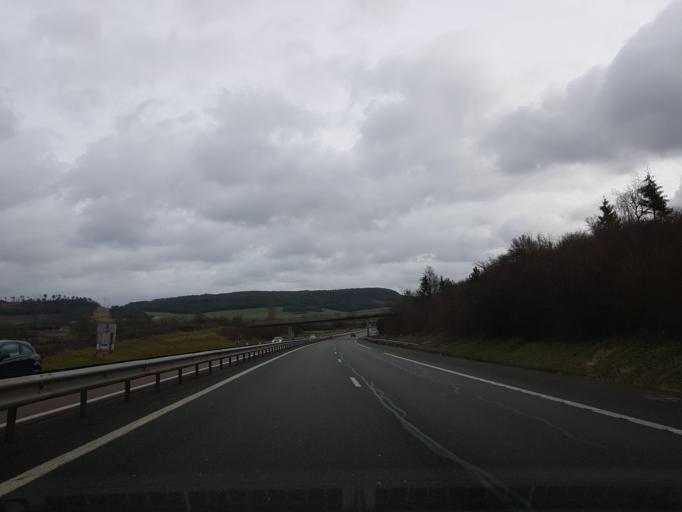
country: FR
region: Champagne-Ardenne
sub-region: Departement de la Haute-Marne
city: Chateauvillain
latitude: 48.0774
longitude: 4.8835
